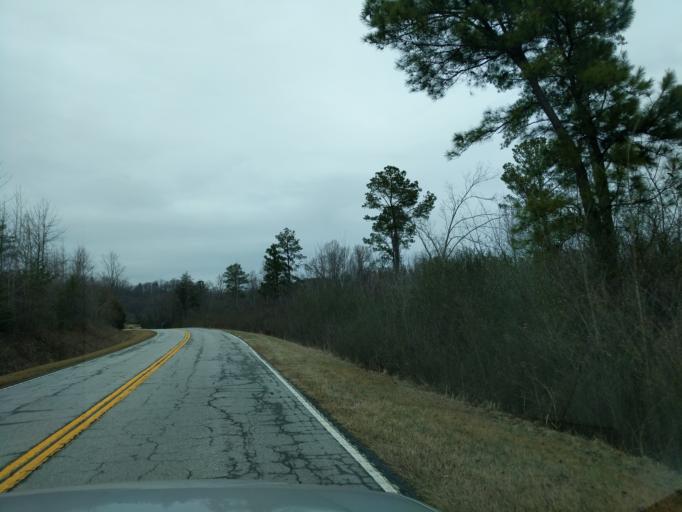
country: US
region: South Carolina
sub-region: Oconee County
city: Walhalla
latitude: 34.7880
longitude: -83.1153
